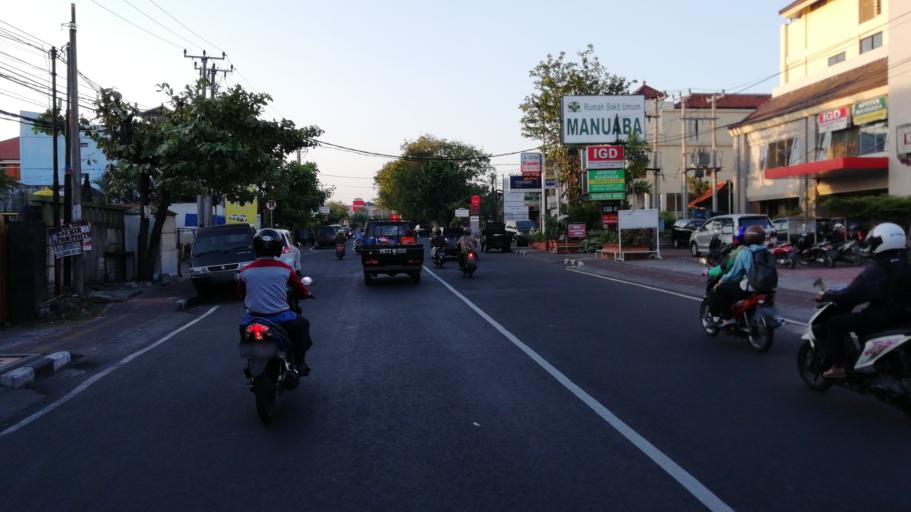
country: ID
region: Bali
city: Denpasar
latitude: -8.6443
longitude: 115.2093
